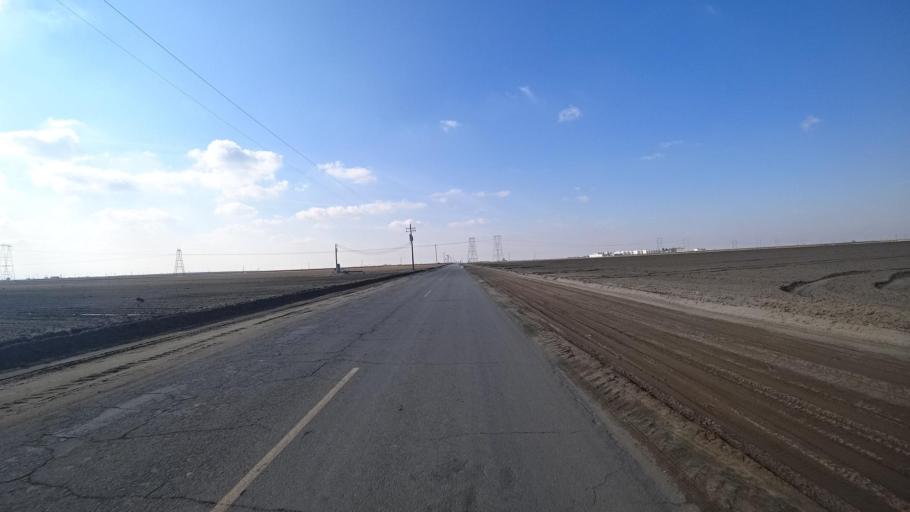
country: US
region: California
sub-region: Kern County
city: Arvin
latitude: 35.2529
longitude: -118.8191
